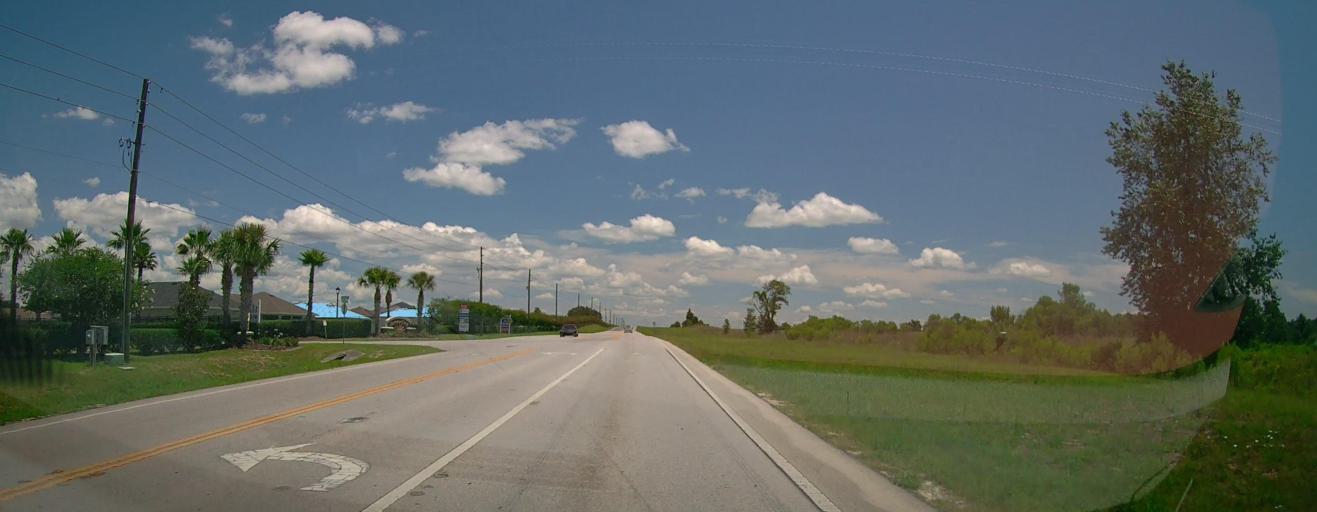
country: US
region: Florida
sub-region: Marion County
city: Belleview
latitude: 29.0864
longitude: -82.0641
